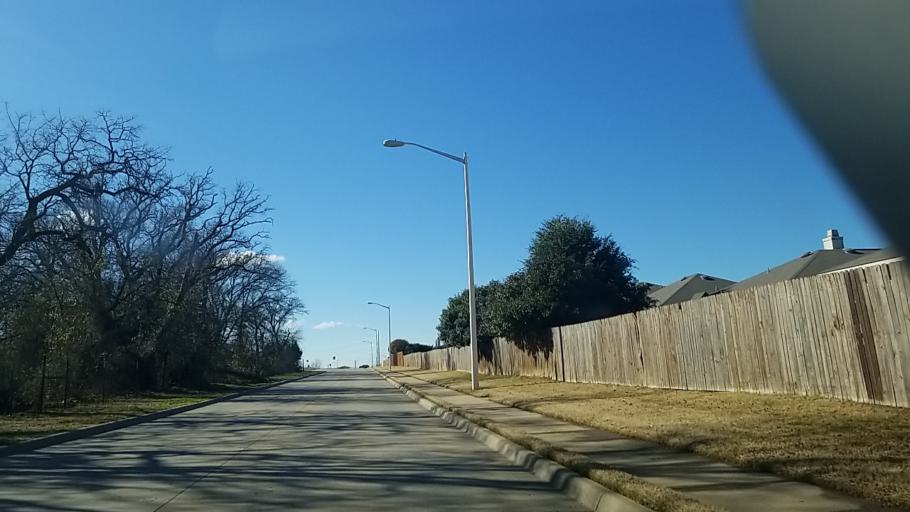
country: US
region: Texas
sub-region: Denton County
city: Corinth
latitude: 33.1468
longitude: -97.0997
